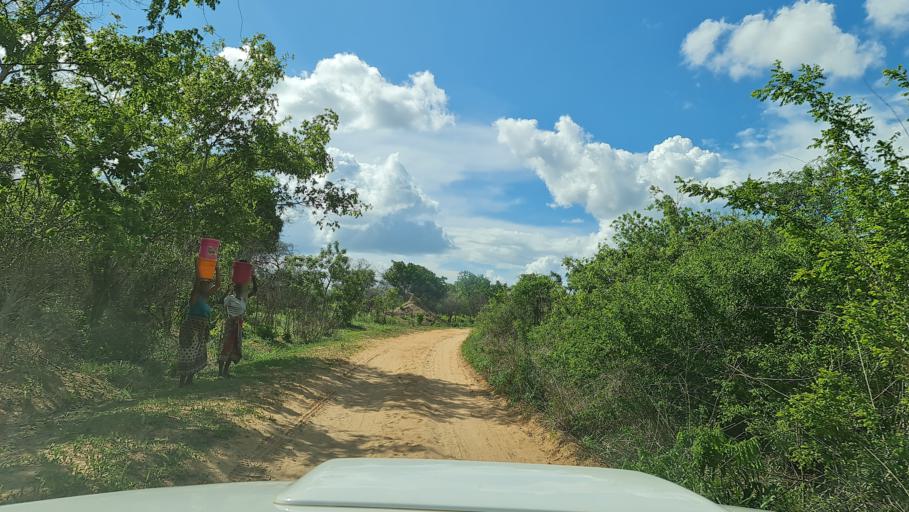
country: MZ
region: Nampula
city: Ilha de Mocambique
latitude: -15.4349
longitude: 40.2769
